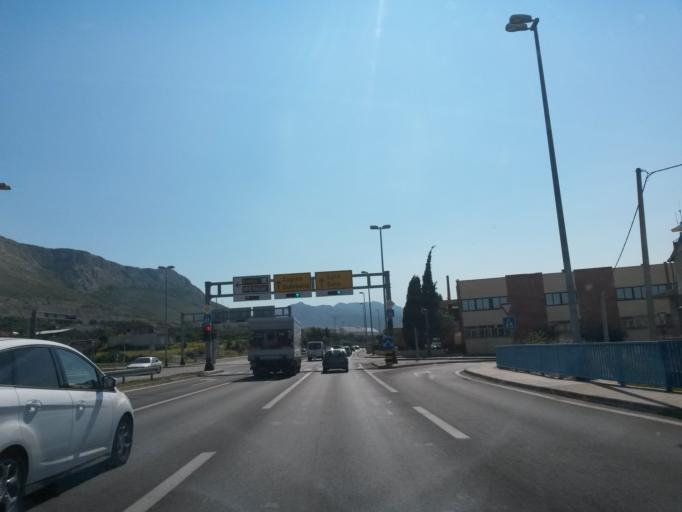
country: HR
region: Splitsko-Dalmatinska
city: Vranjic
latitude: 43.5510
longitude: 16.4282
